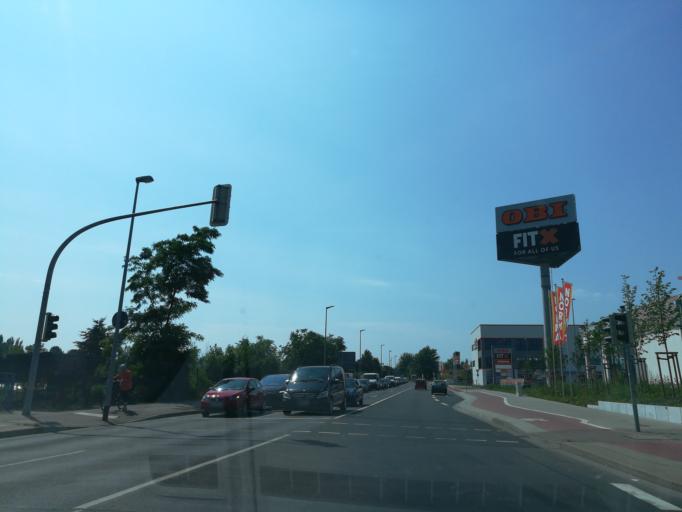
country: DE
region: Saxony-Anhalt
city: Magdeburg
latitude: 52.1031
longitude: 11.6031
